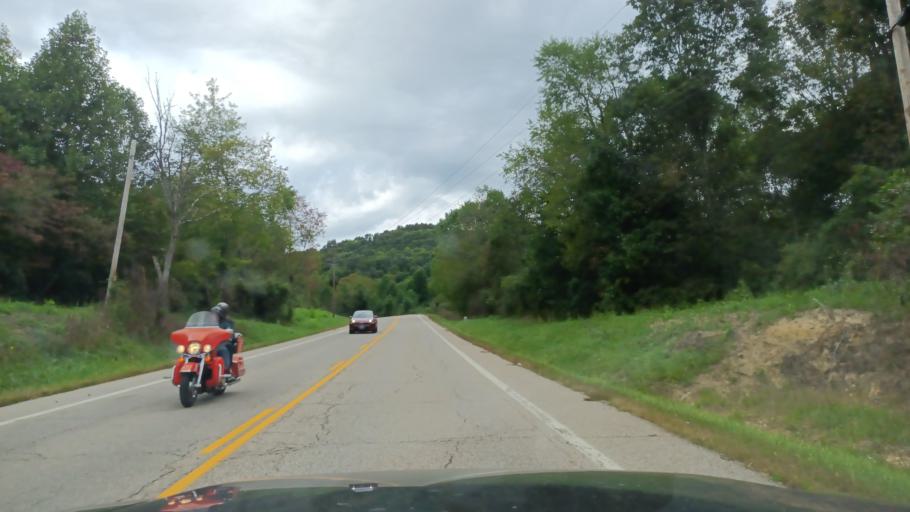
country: US
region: Ohio
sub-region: Vinton County
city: McArthur
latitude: 39.2420
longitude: -82.4536
